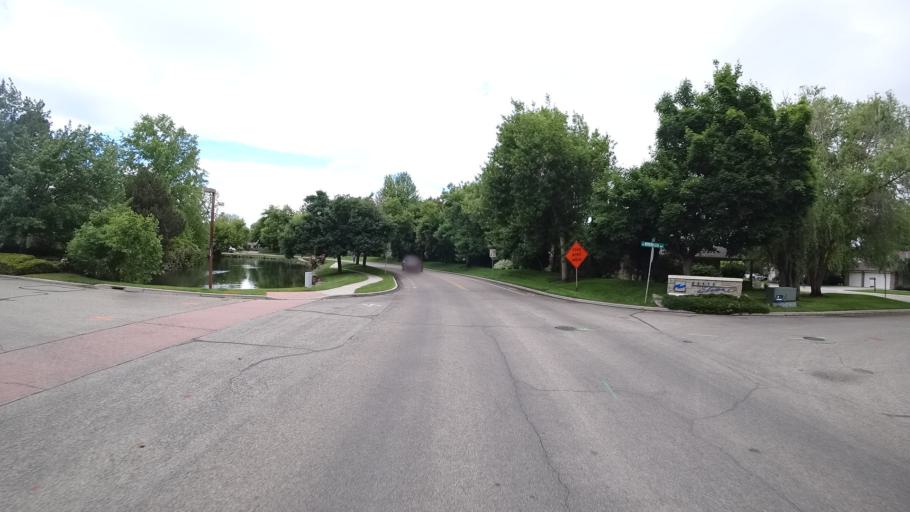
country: US
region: Idaho
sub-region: Ada County
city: Garden City
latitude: 43.6648
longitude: -116.2857
